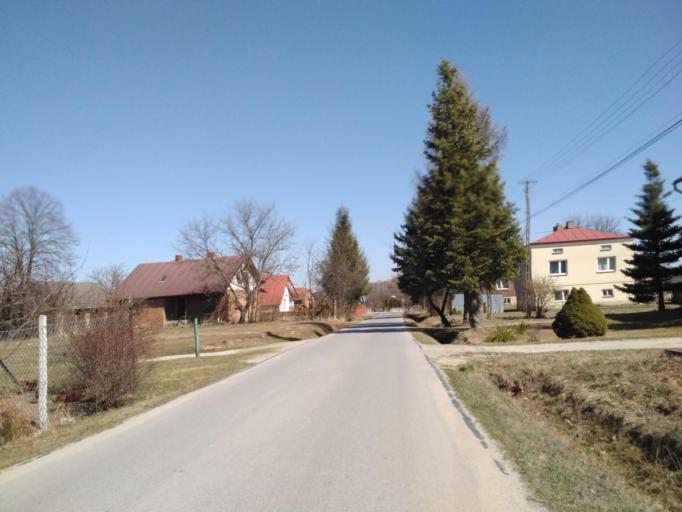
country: PL
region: Subcarpathian Voivodeship
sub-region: Powiat brzozowski
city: Orzechowka
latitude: 49.7235
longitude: 21.9401
